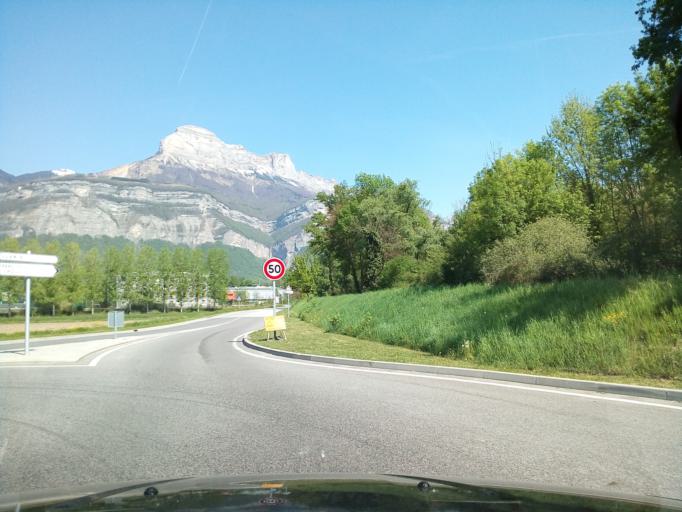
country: FR
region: Rhone-Alpes
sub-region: Departement de l'Isere
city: Villard-Bonnot
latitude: 45.2591
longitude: 5.8832
